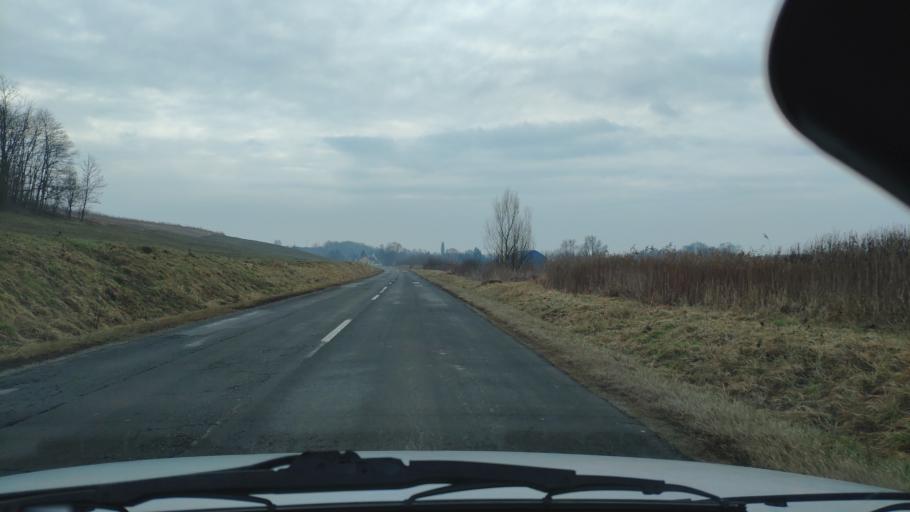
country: HU
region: Zala
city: Nagykanizsa
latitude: 46.5253
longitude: 16.9820
